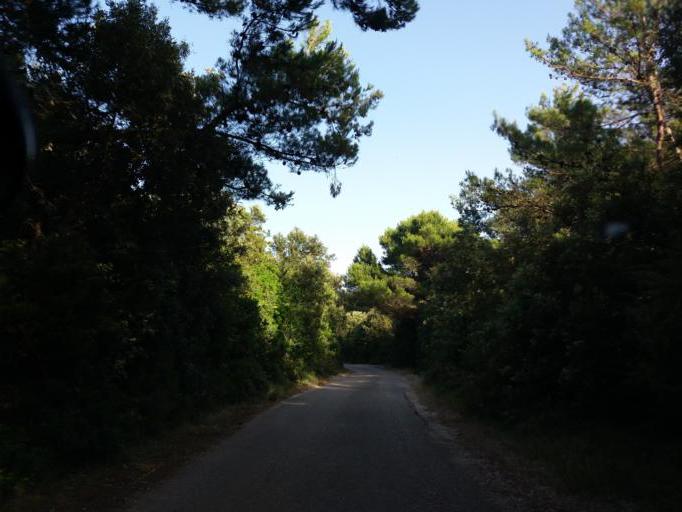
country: HR
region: Zadarska
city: Ugljan
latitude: 44.1483
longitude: 14.8317
